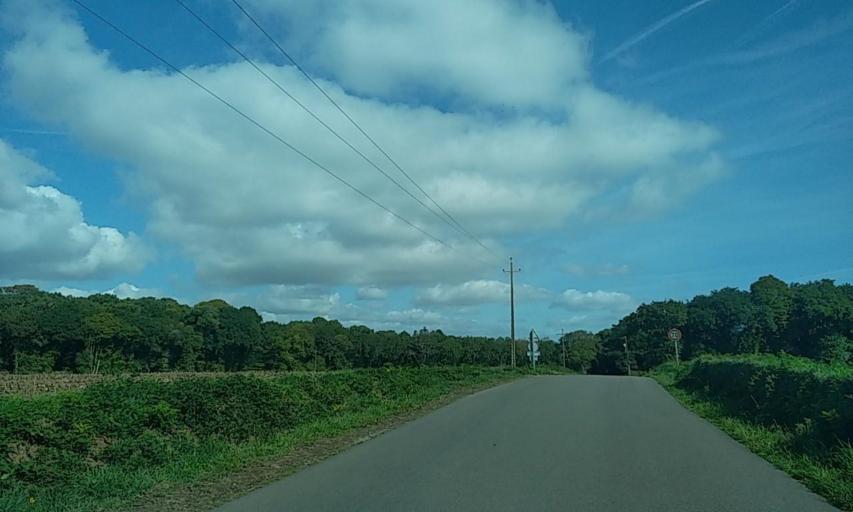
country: FR
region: Brittany
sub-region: Departement du Morbihan
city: Ploemeur
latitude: 47.7232
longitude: -3.4411
